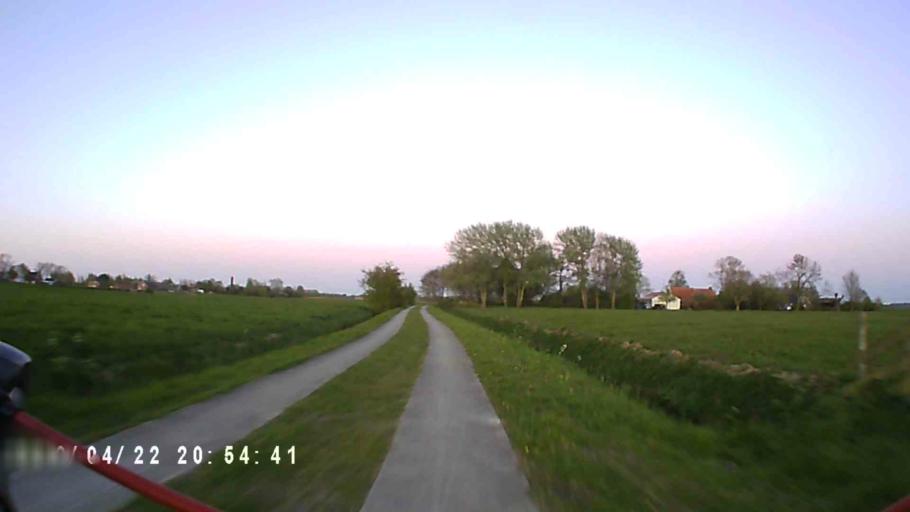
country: NL
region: Groningen
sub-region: Gemeente Winsum
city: Winsum
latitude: 53.3323
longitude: 6.5573
